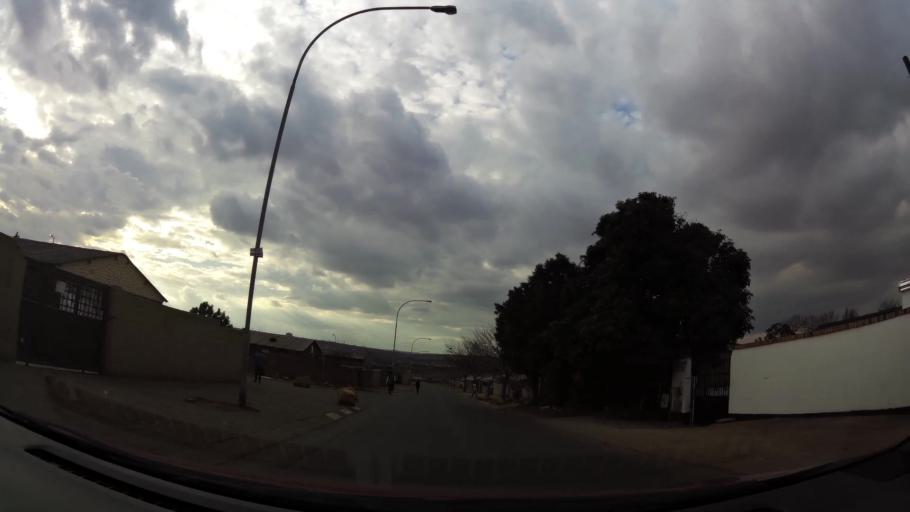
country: ZA
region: Gauteng
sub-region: City of Johannesburg Metropolitan Municipality
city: Soweto
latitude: -26.2429
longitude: 27.8158
